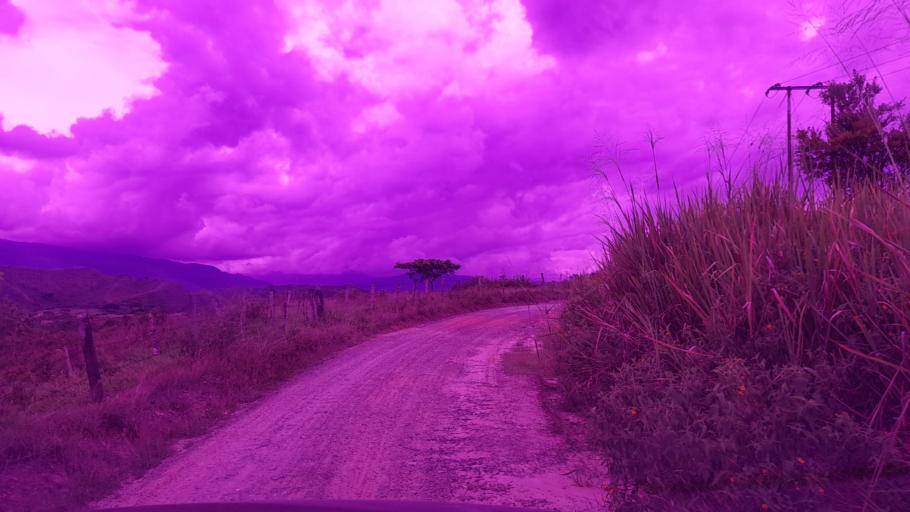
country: CO
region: Valle del Cauca
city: Bugalagrande
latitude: 4.1868
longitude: -76.1374
